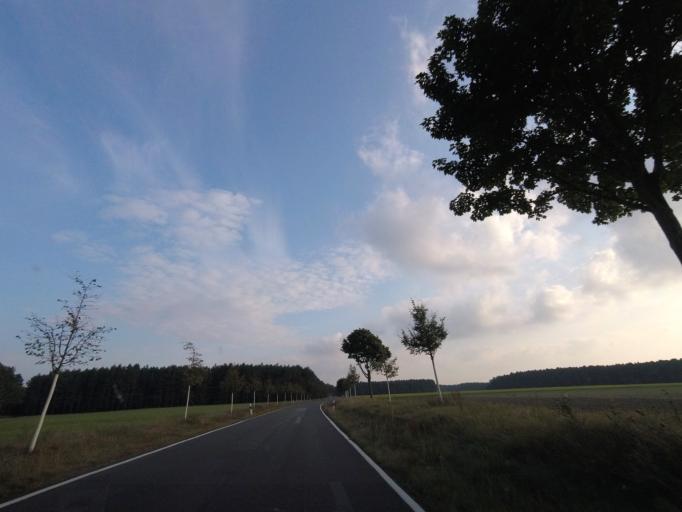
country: DE
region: Brandenburg
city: Treuenbrietzen
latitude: 52.1298
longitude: 12.8608
